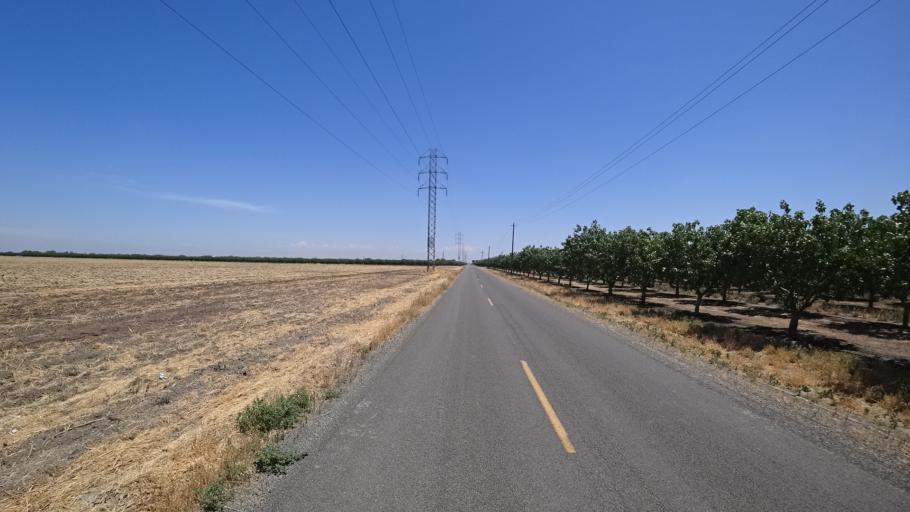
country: US
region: California
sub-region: Kings County
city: Corcoran
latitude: 36.1088
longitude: -119.5477
